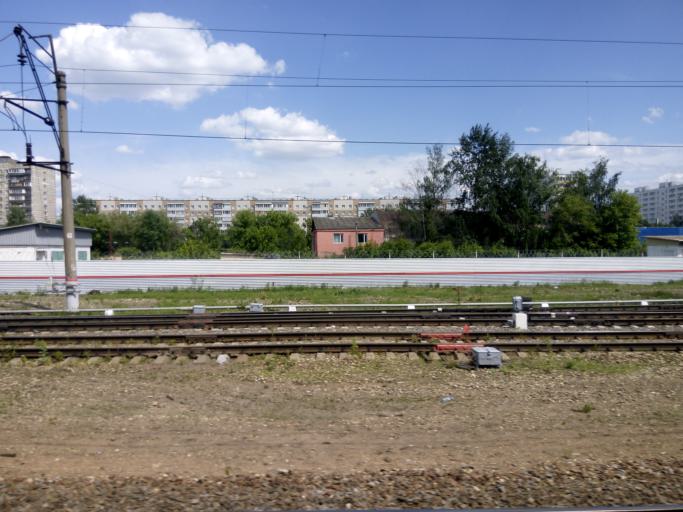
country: RU
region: Moskovskaya
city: Biryulevo Zapadnoye
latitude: 55.5985
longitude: 37.6506
